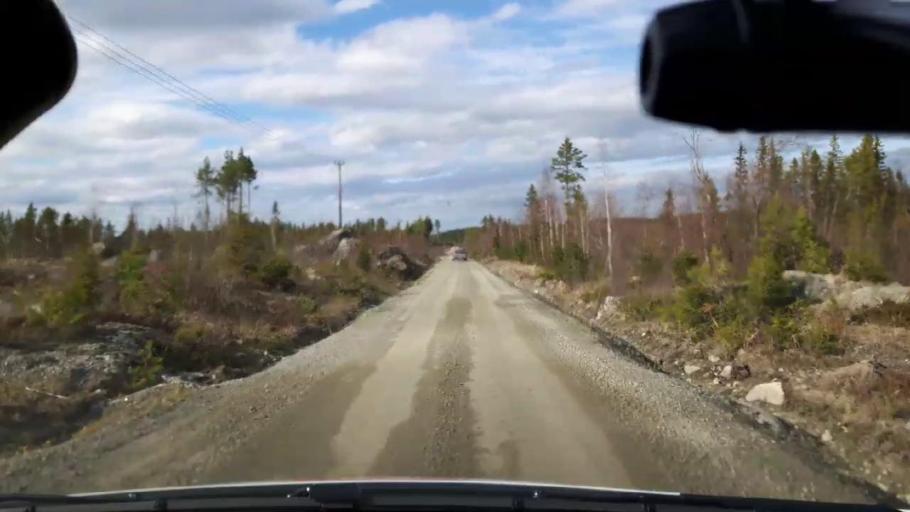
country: SE
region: Jaemtland
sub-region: Bergs Kommun
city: Hoverberg
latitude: 62.8408
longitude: 14.6669
